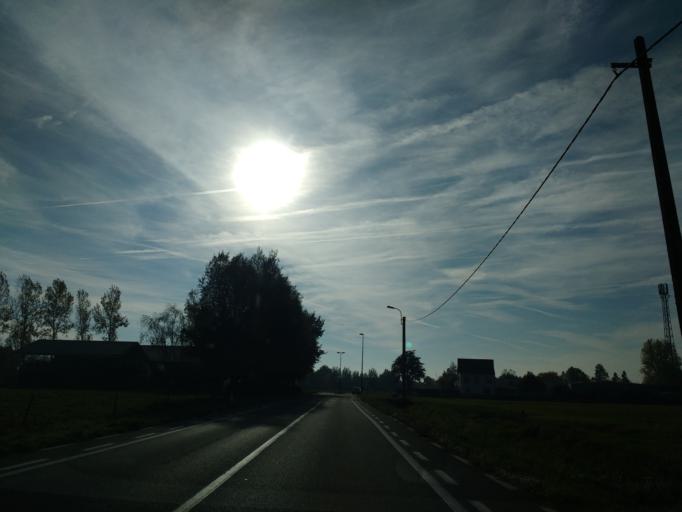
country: BE
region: Flanders
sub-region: Provincie Oost-Vlaanderen
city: Kaprijke
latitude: 51.2305
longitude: 3.6195
